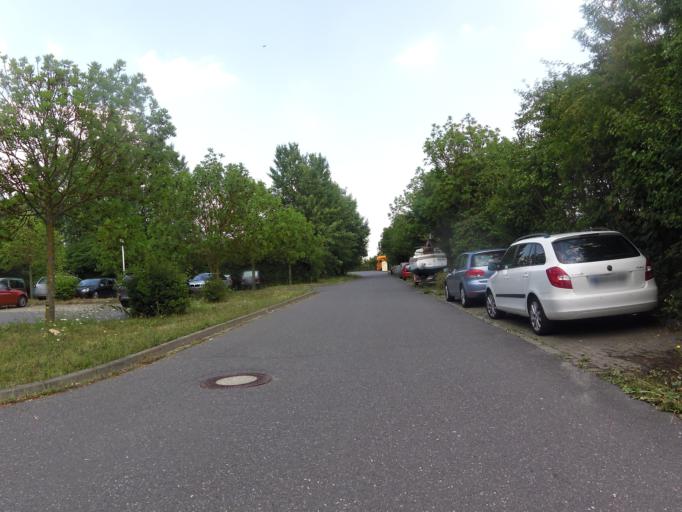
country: DE
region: Bavaria
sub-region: Regierungsbezirk Unterfranken
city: Randersacker
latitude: 49.7323
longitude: 9.9679
